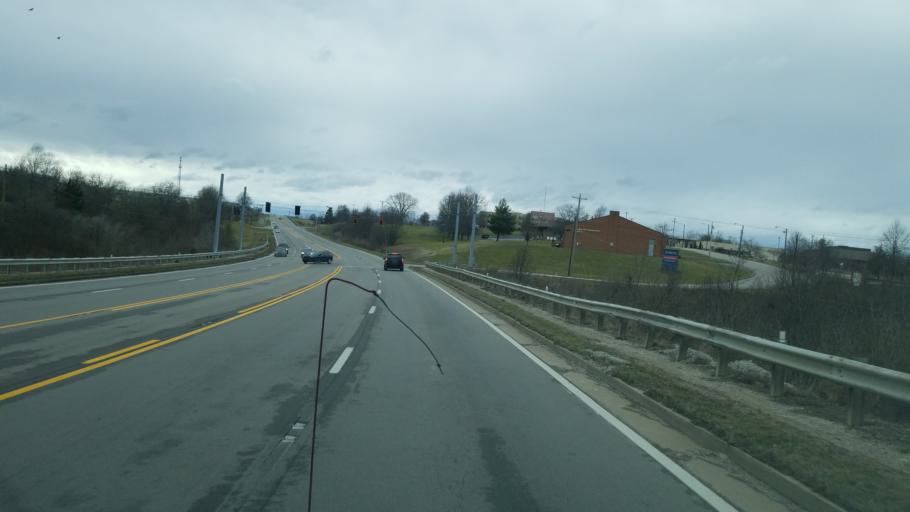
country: US
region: Ohio
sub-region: Brown County
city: Aberdeen
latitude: 38.6366
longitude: -83.8026
